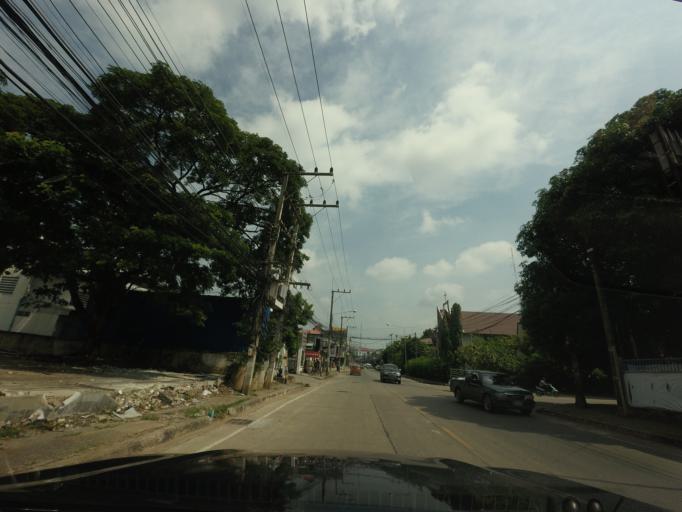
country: TH
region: Khon Kaen
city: Khon Kaen
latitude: 16.4356
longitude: 102.8298
